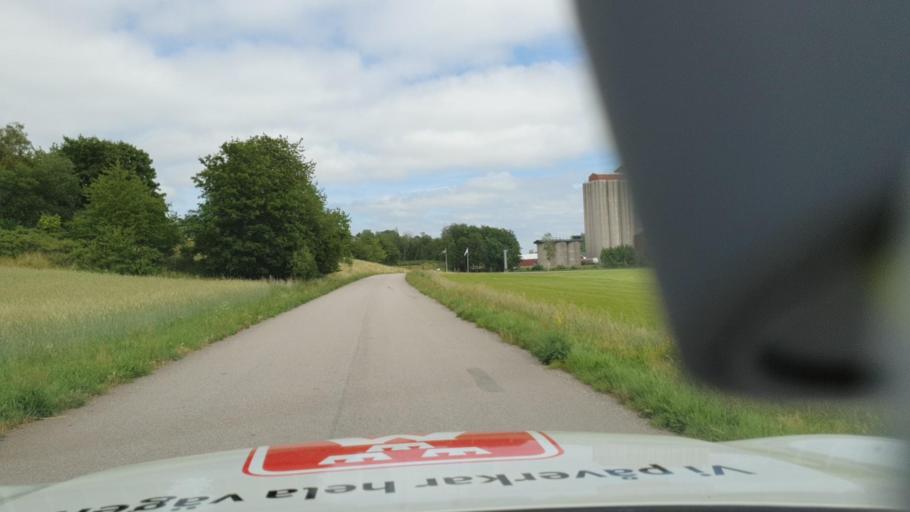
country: SE
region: Vaestra Goetaland
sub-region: Gotene Kommun
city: Kallby
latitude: 58.5437
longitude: 13.3840
